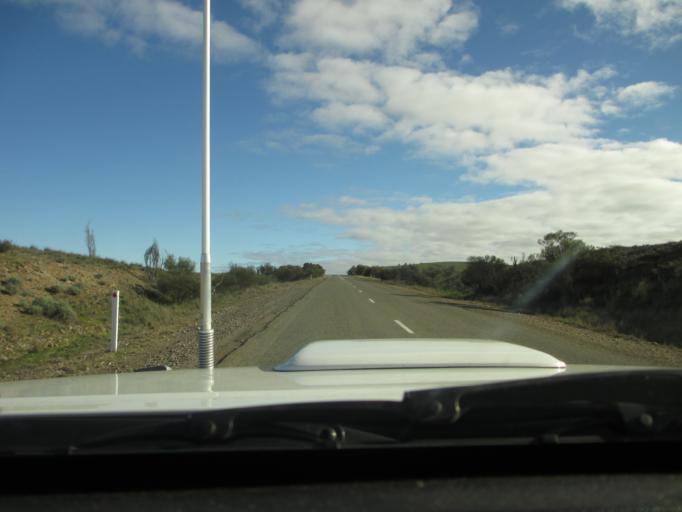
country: AU
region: South Australia
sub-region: Peterborough
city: Peterborough
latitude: -32.6236
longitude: 138.5820
